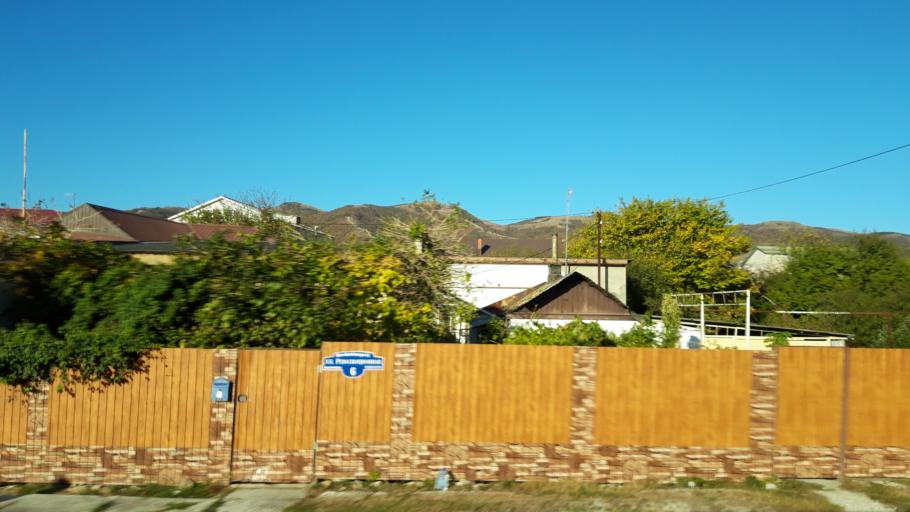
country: RU
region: Krasnodarskiy
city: Kabardinka
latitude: 44.6468
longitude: 37.9530
